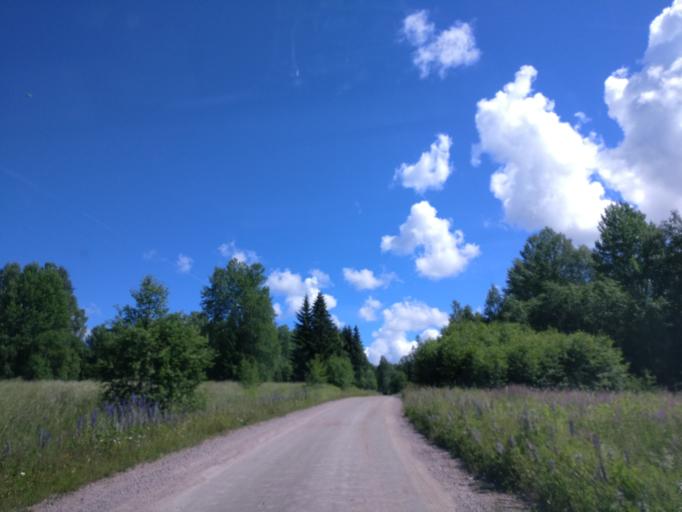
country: SE
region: Vaermland
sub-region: Hagfors Kommun
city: Hagfors
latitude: 60.0406
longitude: 13.6479
